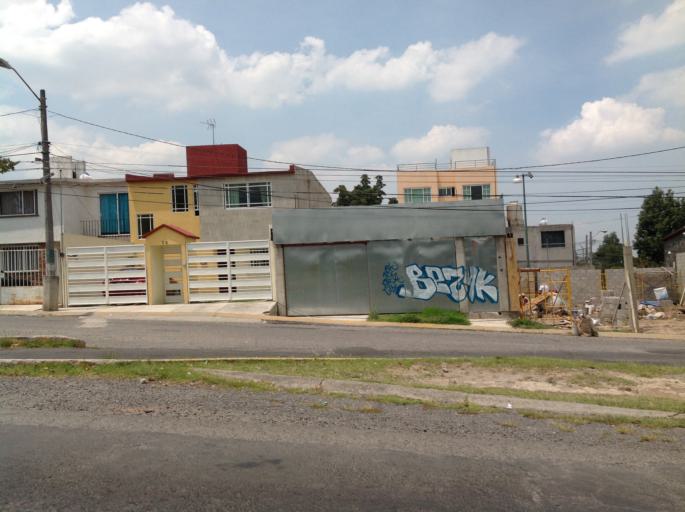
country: MX
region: Mexico
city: Ciudad Lopez Mateos
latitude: 19.5936
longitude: -99.2303
